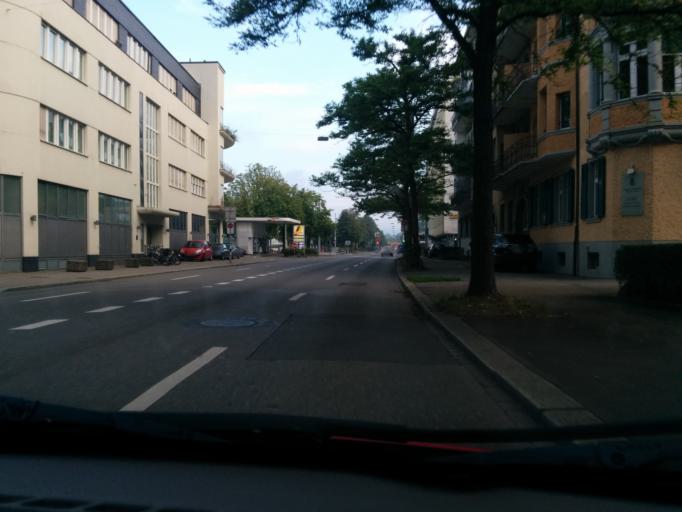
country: CH
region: Zurich
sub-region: Bezirk Zuerich
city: Zurich
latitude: 47.3607
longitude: 8.5485
